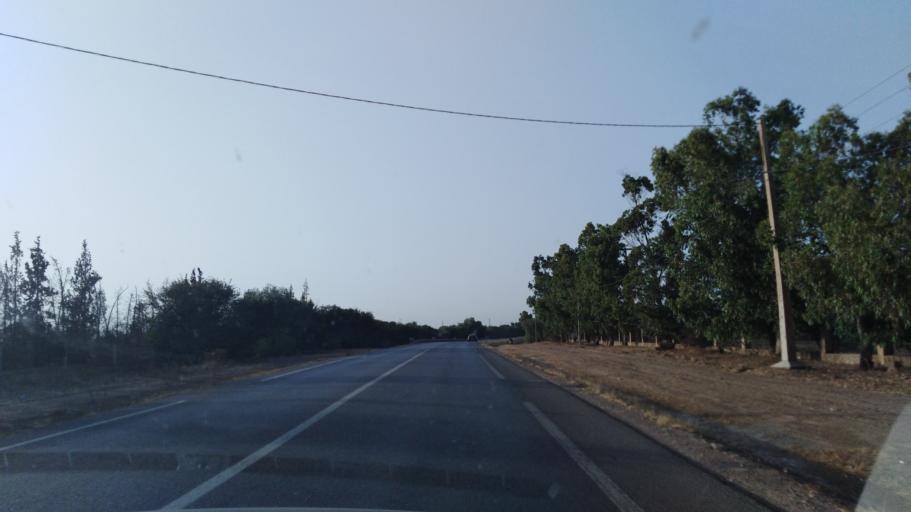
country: MA
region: Chaouia-Ouardigha
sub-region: Settat Province
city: Berrechid
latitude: 33.1834
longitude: -7.6158
